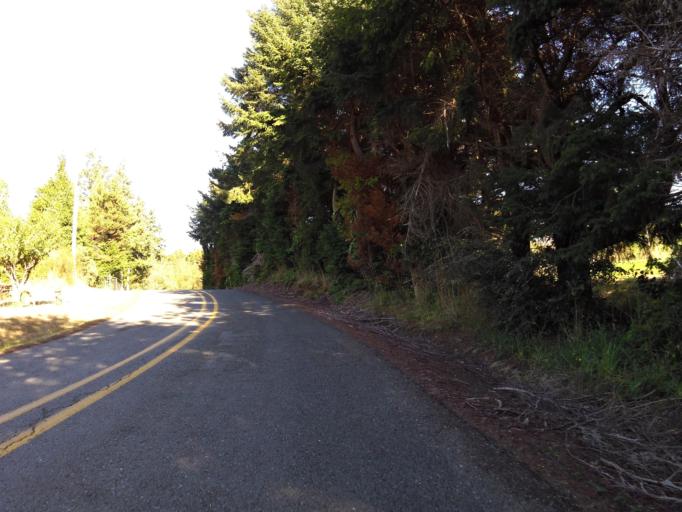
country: US
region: Oregon
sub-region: Coos County
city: Bandon
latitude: 43.0394
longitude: -124.4037
